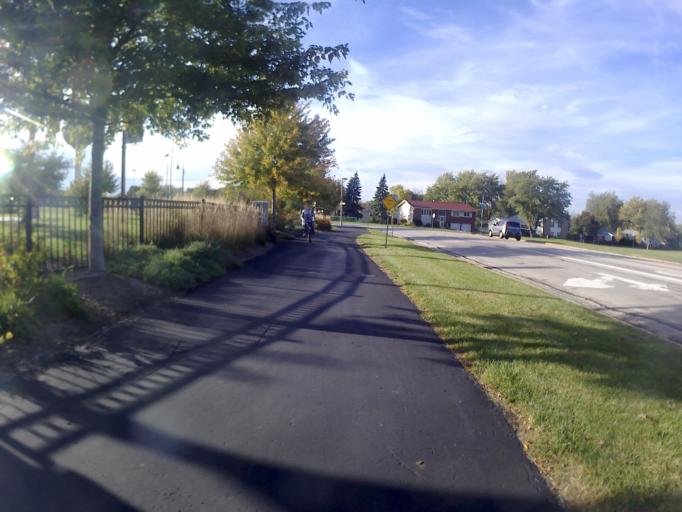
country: US
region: Illinois
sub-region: DuPage County
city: Woodridge
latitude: 41.7653
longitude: -88.0568
